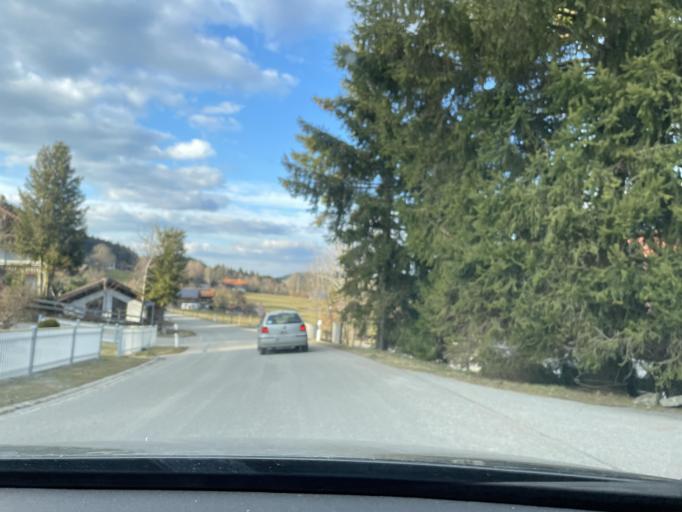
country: DE
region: Bavaria
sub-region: Lower Bavaria
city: Kollnburg
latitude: 49.0336
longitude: 12.8666
